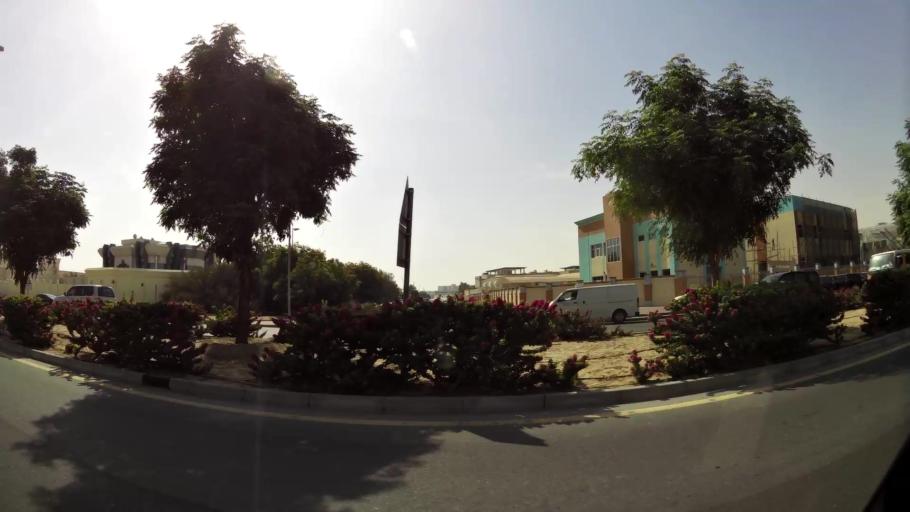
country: AE
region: Ash Shariqah
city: Sharjah
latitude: 25.2398
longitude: 55.4264
